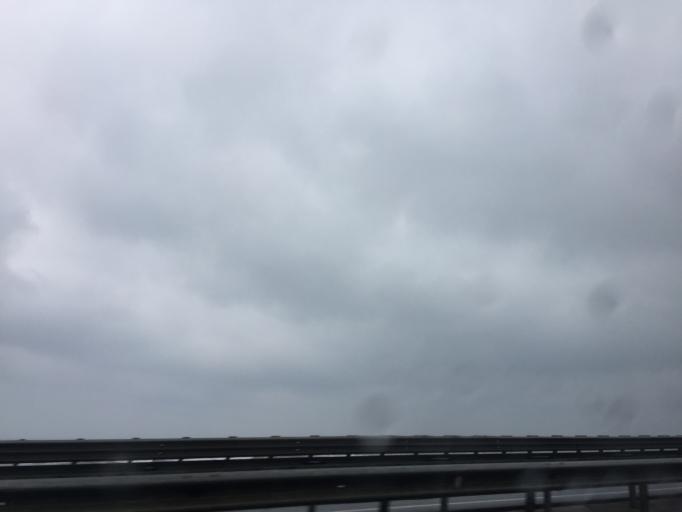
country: TR
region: Duzce
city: Akcakoca
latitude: 41.1004
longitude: 31.2332
